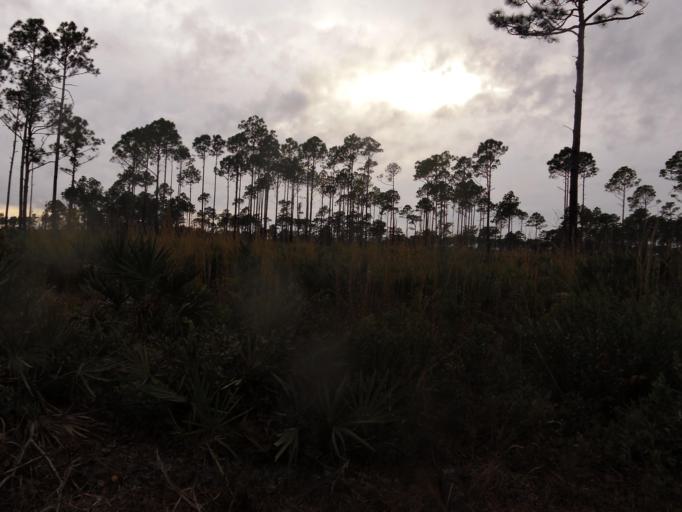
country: US
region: Florida
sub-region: Duval County
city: Atlantic Beach
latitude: 30.4778
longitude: -81.4987
